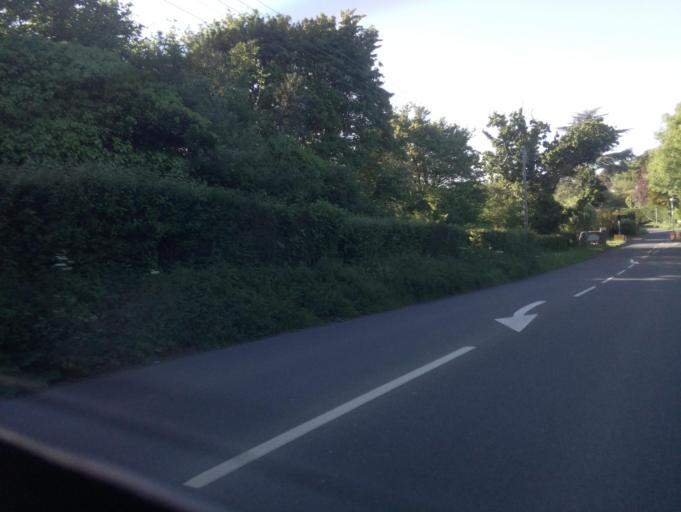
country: GB
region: England
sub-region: Devon
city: Colyton
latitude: 50.7236
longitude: -3.0715
